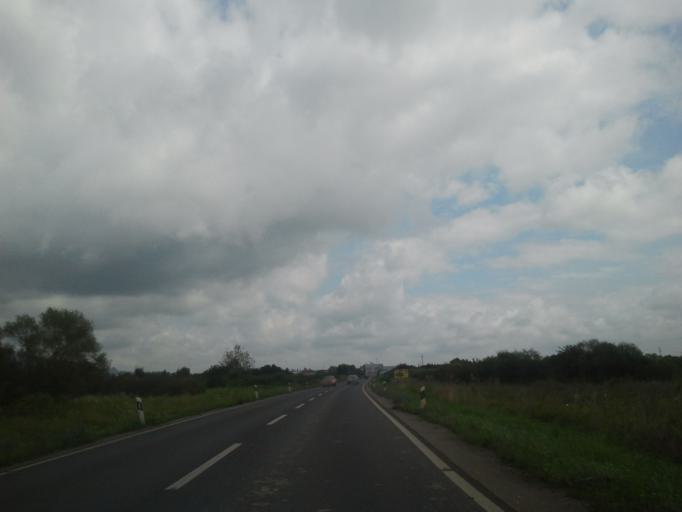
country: HR
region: Zagrebacka
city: Jastrebarsko
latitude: 45.6531
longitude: 15.6323
